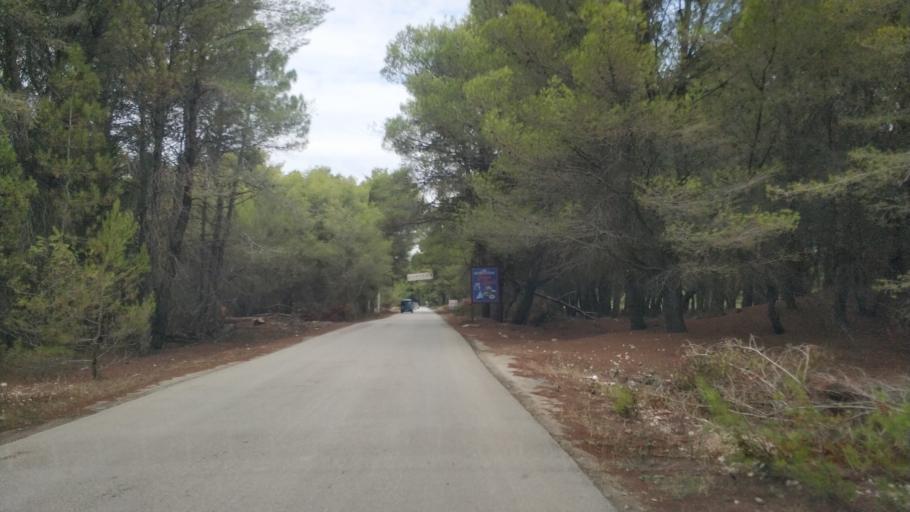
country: AL
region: Vlore
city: Vlore
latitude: 40.4872
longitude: 19.4436
